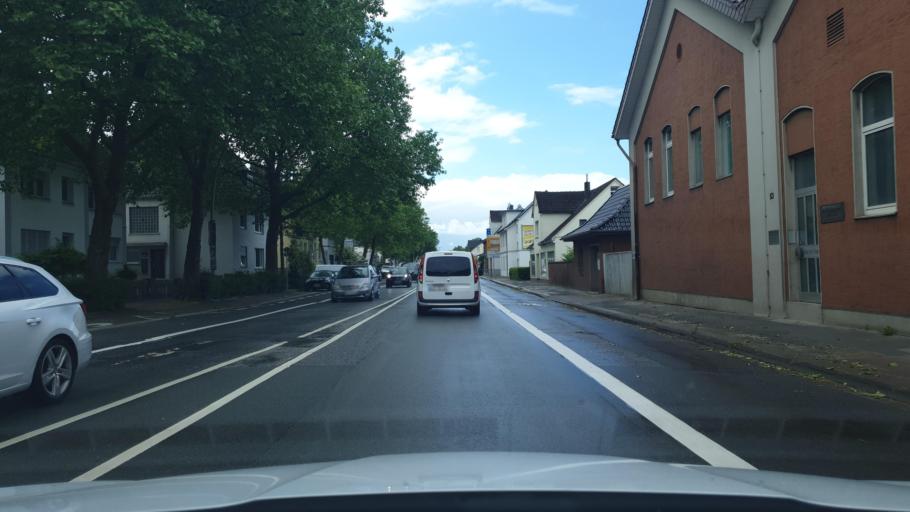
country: DE
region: North Rhine-Westphalia
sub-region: Regierungsbezirk Detmold
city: Herford
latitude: 52.1234
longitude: 8.6821
